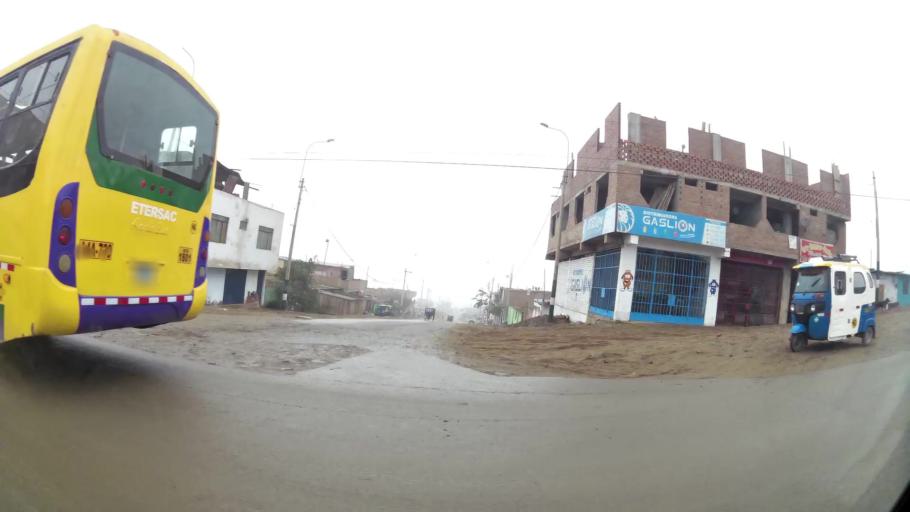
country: PE
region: Lima
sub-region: Lima
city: Santa Rosa
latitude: -11.8314
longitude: -77.1488
